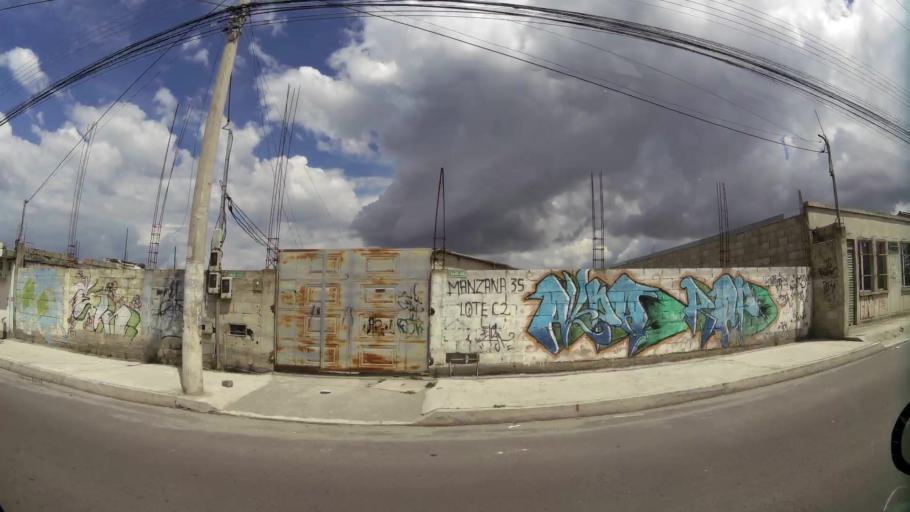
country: EC
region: Pichincha
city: Quito
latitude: -0.0640
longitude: -78.4183
